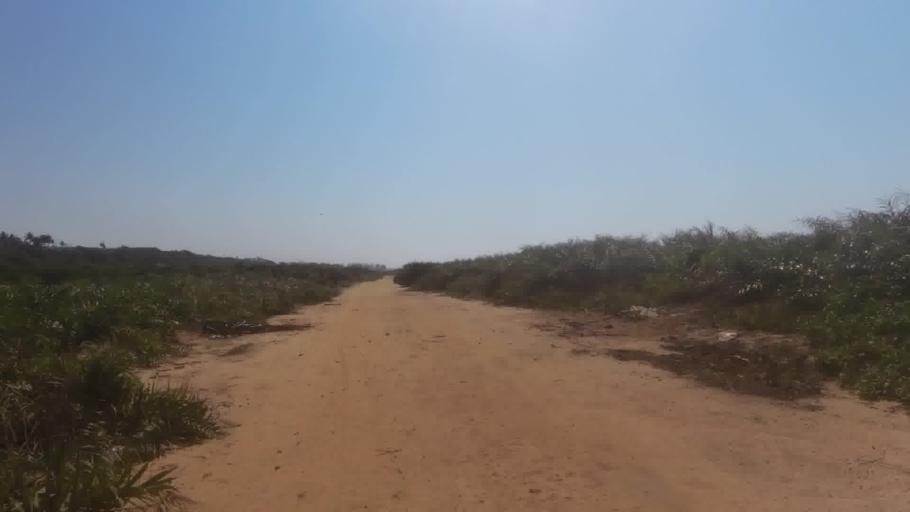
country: BR
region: Espirito Santo
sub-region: Marataizes
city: Marataizes
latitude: -21.0866
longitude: -40.8422
